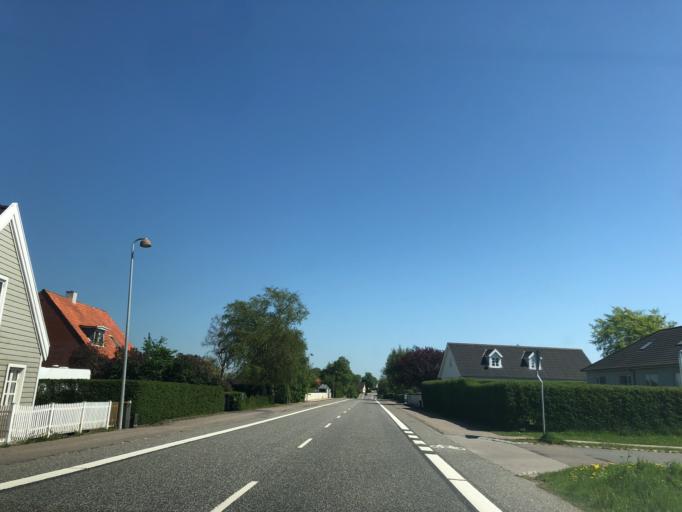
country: DK
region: Zealand
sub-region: Slagelse Kommune
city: Skaelskor
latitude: 55.3052
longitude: 11.2602
